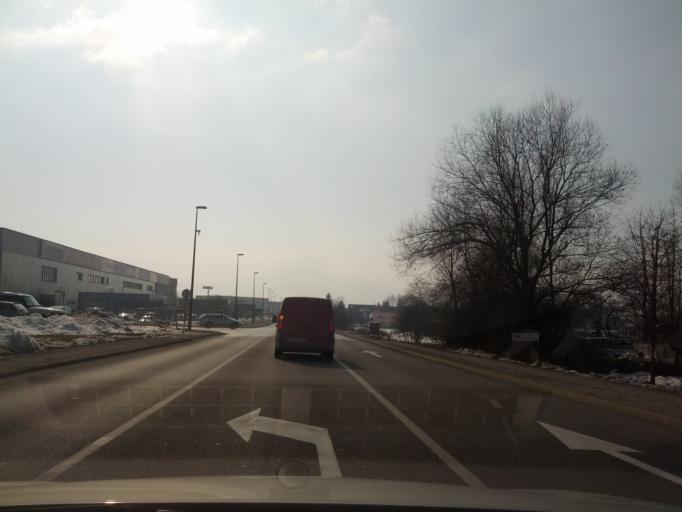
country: SI
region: Skofljica
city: Lavrica
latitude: 46.0243
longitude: 14.5362
